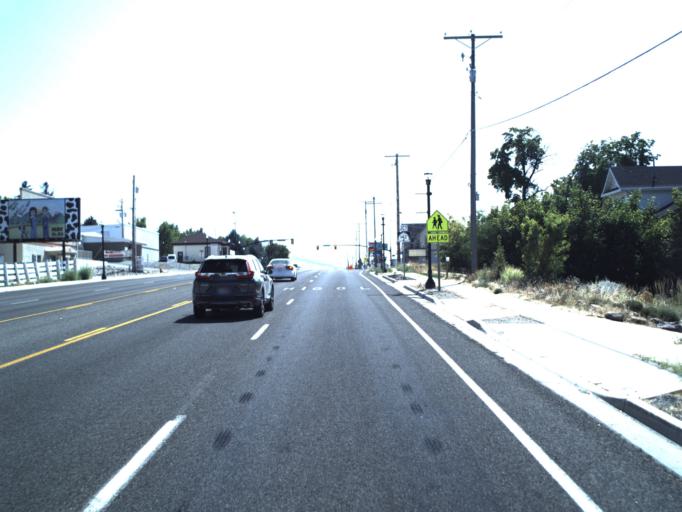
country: US
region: Utah
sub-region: Cache County
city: Richmond
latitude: 41.9247
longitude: -111.8144
